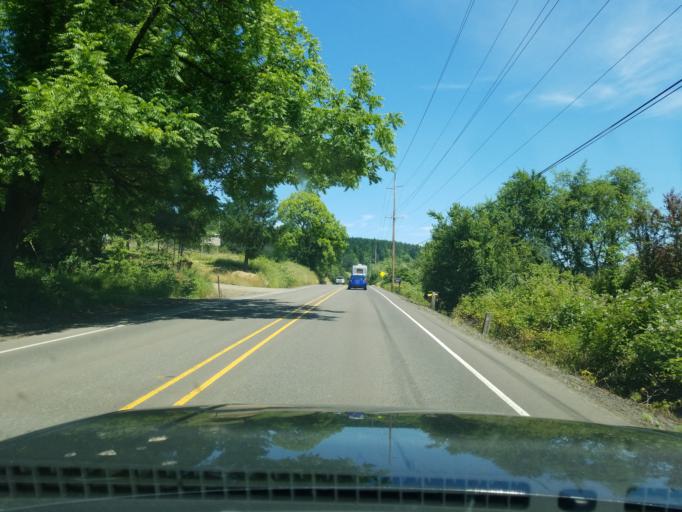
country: US
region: Oregon
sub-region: Yamhill County
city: Yamhill
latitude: 45.3907
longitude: -123.1369
